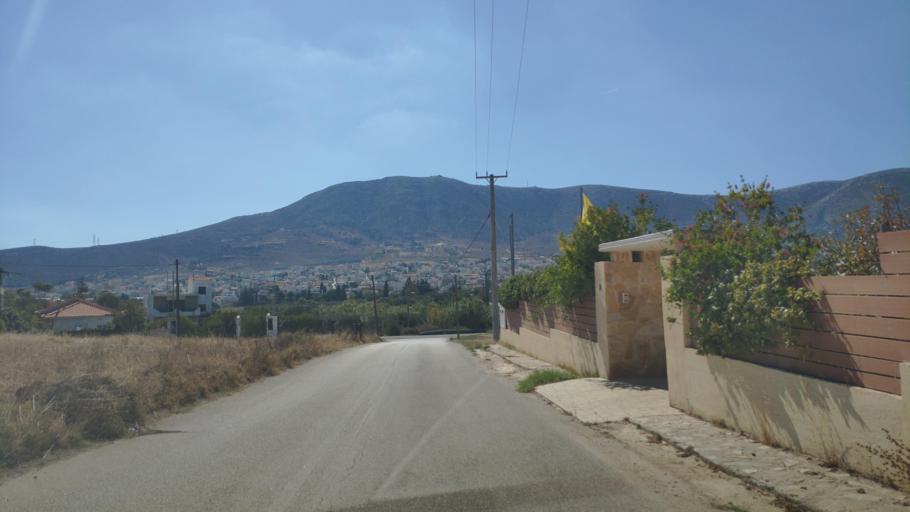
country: GR
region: Attica
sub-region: Nomarchia Anatolikis Attikis
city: Keratea
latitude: 37.8141
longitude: 23.9867
